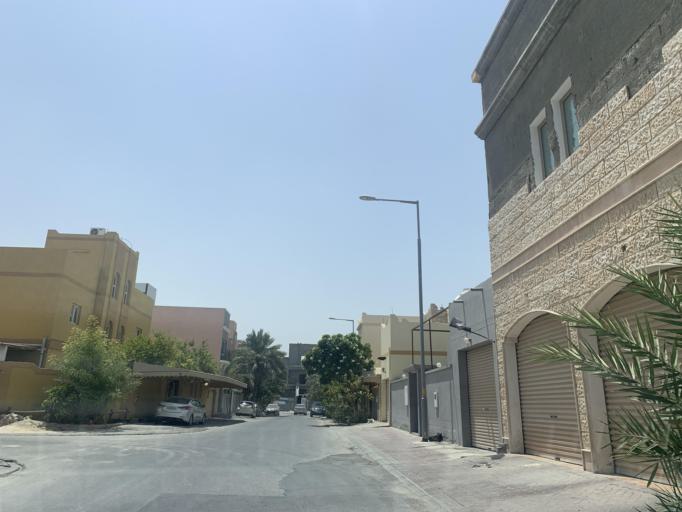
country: BH
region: Central Governorate
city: Madinat Hamad
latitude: 26.1449
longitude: 50.5027
